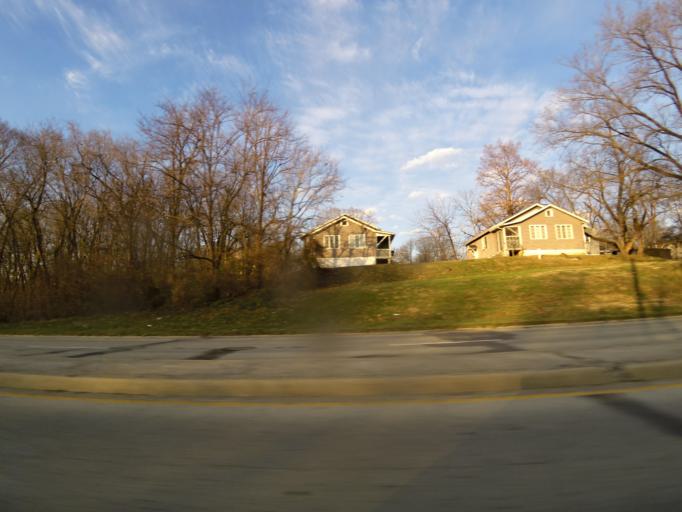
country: US
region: Illinois
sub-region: Fayette County
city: Vandalia
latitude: 38.9681
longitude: -89.0932
